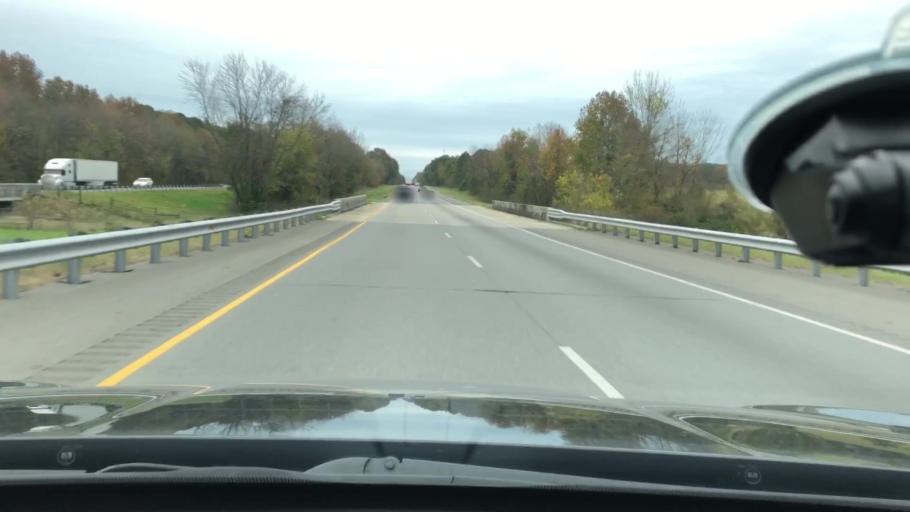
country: US
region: Arkansas
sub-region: Hempstead County
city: Hope
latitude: 33.6396
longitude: -93.6996
